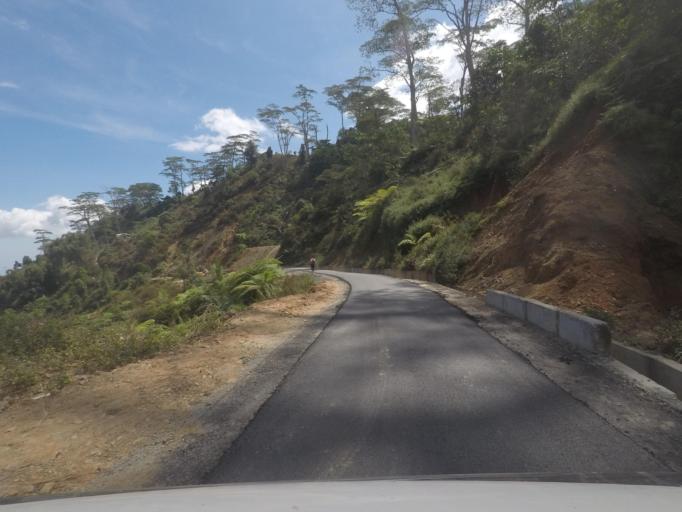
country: TL
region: Ermera
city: Gleno
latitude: -8.7528
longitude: 125.3330
